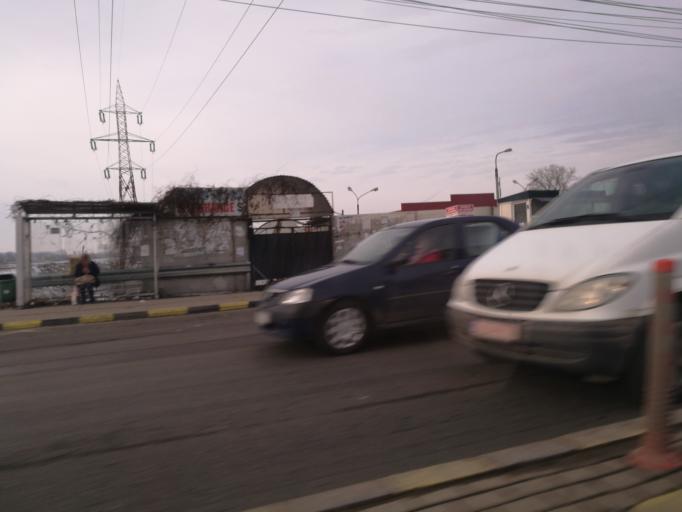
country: RO
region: Suceava
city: Suceava
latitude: 47.6594
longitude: 26.2647
